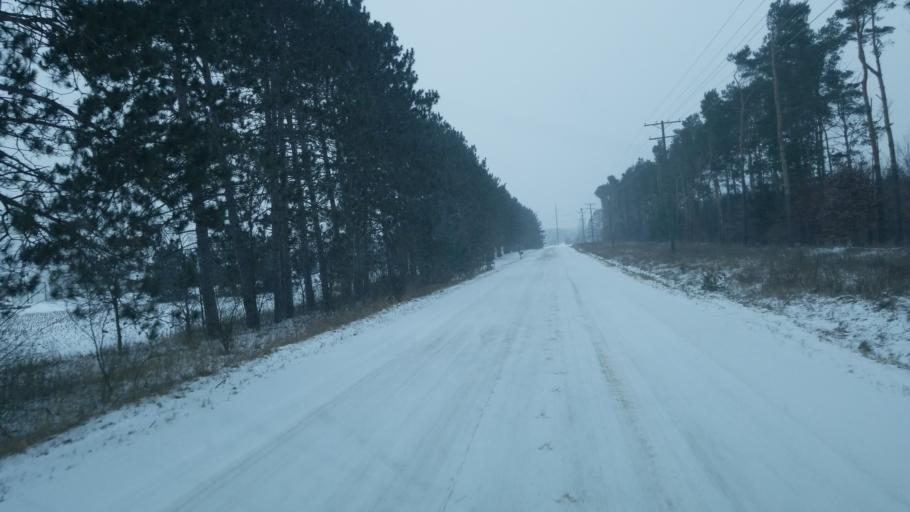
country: US
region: Michigan
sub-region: Osceola County
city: Reed City
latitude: 43.8291
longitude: -85.4193
